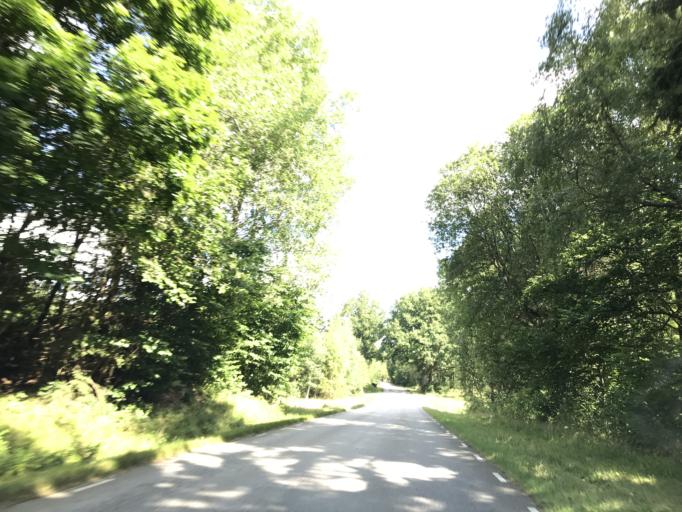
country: SE
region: Halland
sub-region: Laholms Kommun
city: Knared
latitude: 56.4446
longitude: 13.3146
